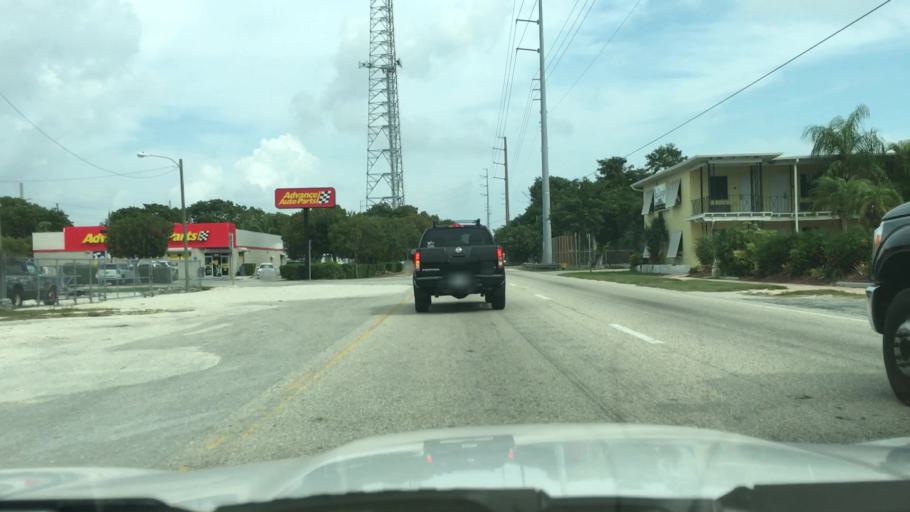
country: US
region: Florida
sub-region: Monroe County
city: Key Largo
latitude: 25.0903
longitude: -80.4445
